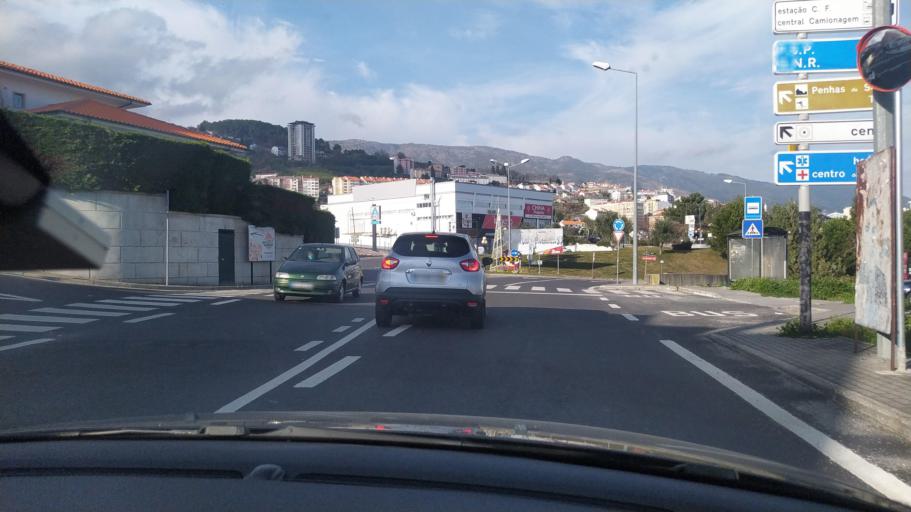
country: PT
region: Castelo Branco
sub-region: Covilha
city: Covilha
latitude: 40.2646
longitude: -7.5036
